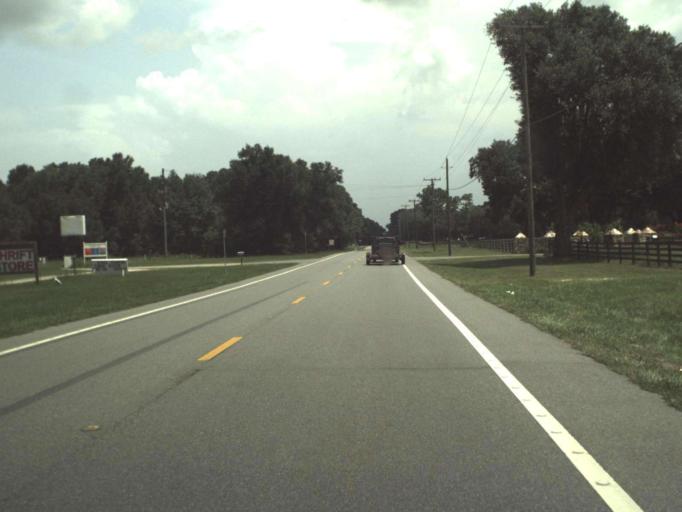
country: US
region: Florida
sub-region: Sumter County
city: Bushnell
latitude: 28.6786
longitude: -82.1042
